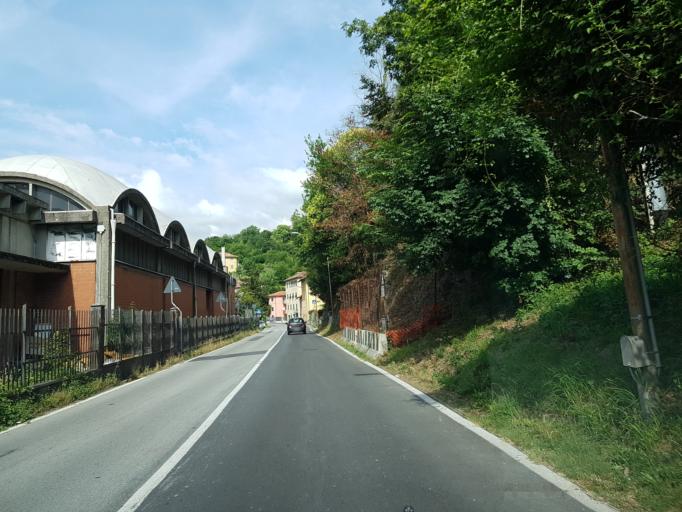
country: IT
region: Liguria
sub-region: Provincia di Genova
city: Manesseno
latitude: 44.4781
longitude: 8.9339
